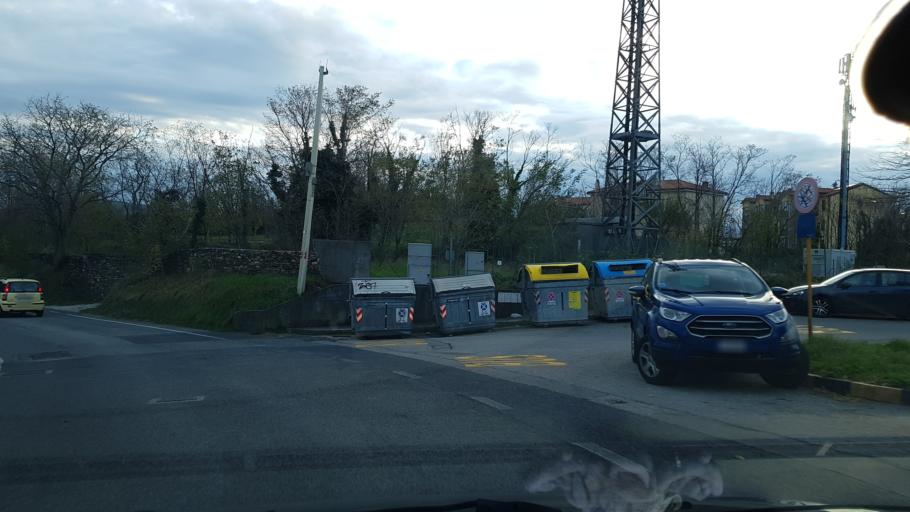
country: IT
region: Friuli Venezia Giulia
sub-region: Provincia di Trieste
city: Trieste
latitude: 45.6279
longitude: 13.8106
